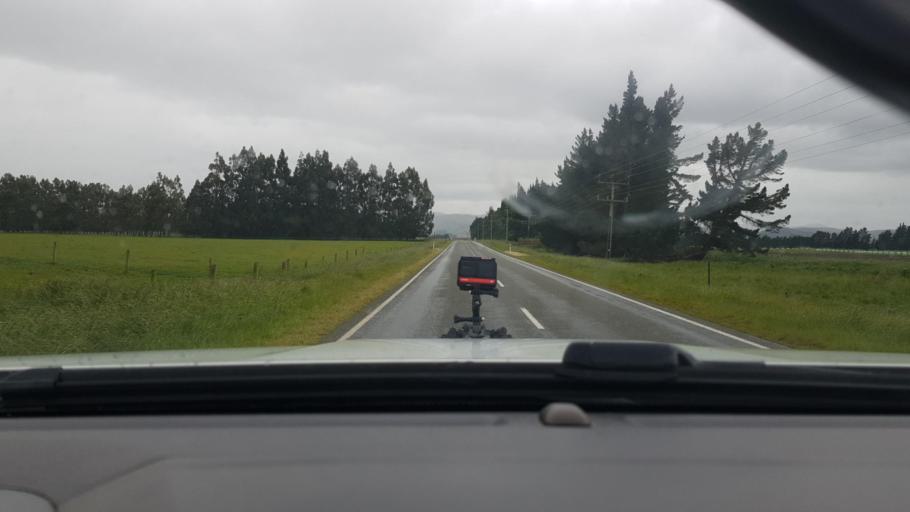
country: NZ
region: Southland
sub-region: Southland District
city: Winton
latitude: -45.7747
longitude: 168.4019
